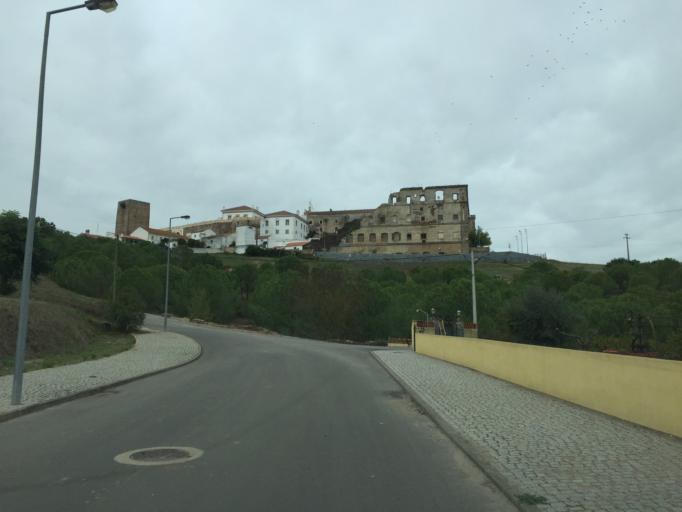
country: PT
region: Portalegre
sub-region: Avis
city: Avis
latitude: 39.0541
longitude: -7.8879
